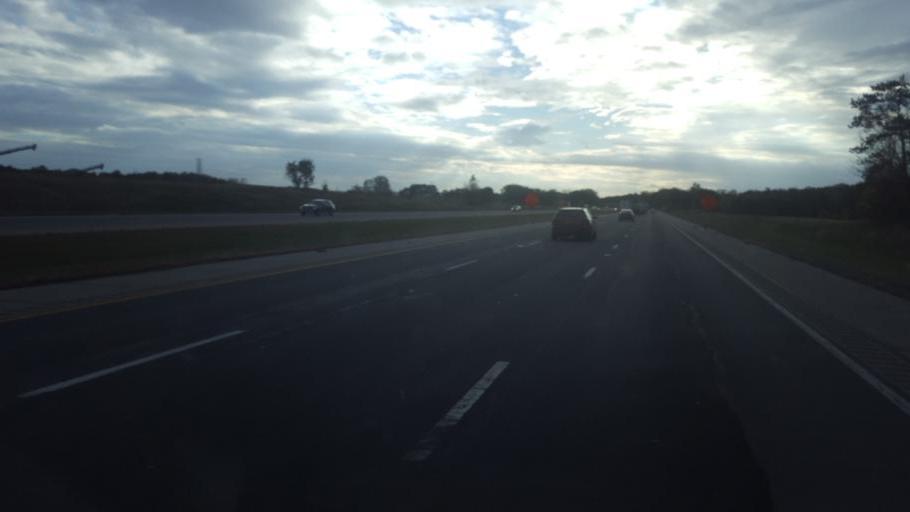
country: US
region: Ohio
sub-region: Ashland County
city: Ashland
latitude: 40.8703
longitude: -82.2313
